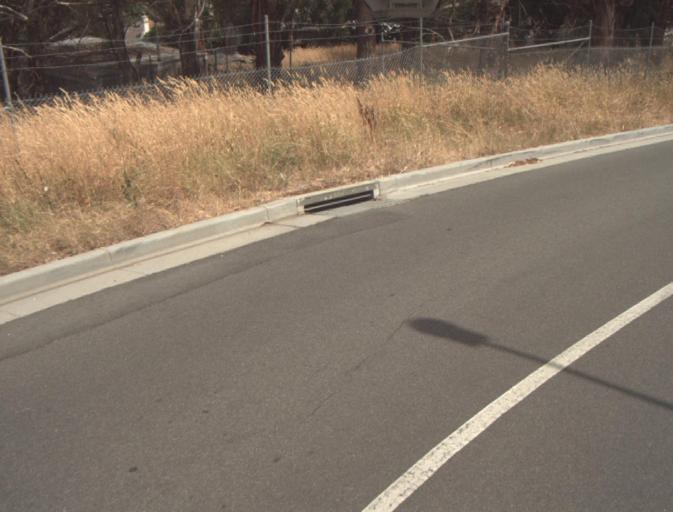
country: AU
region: Tasmania
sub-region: Launceston
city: East Launceston
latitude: -41.4507
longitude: 147.1495
